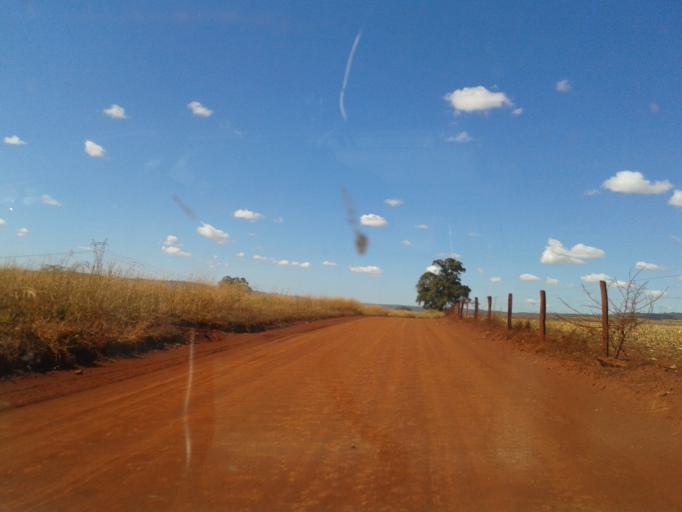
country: BR
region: Minas Gerais
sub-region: Centralina
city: Centralina
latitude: -18.5817
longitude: -49.1310
